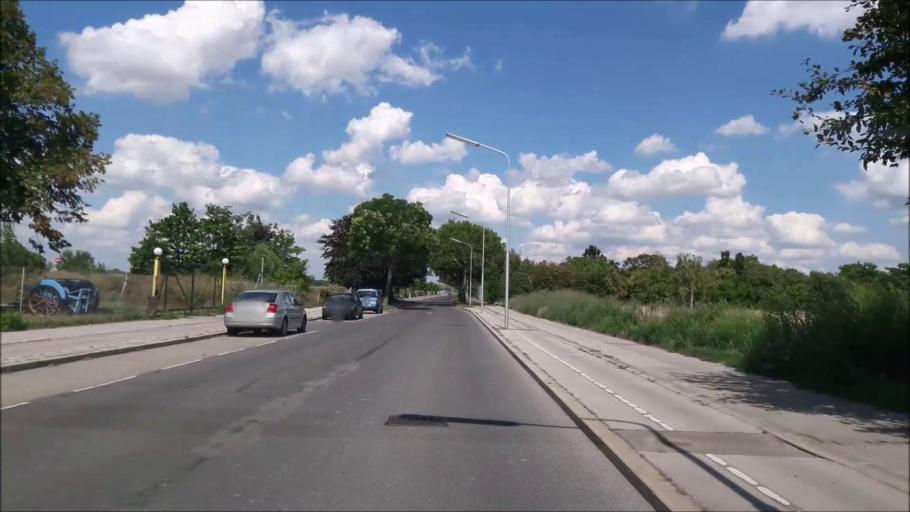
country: AT
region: Lower Austria
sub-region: Politischer Bezirk Wien-Umgebung
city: Gerasdorf bei Wien
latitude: 48.2382
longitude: 16.4644
